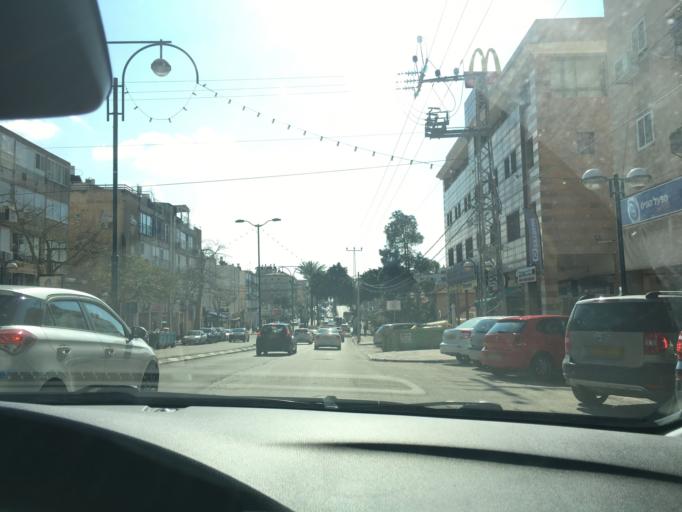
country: IL
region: Tel Aviv
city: Ramat HaSharon
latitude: 32.1478
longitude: 34.8394
